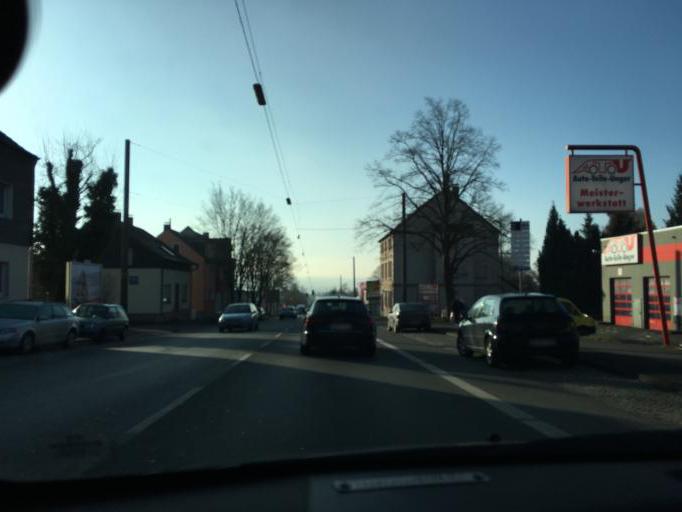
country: DE
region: North Rhine-Westphalia
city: Schwerte
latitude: 51.4523
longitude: 7.5615
